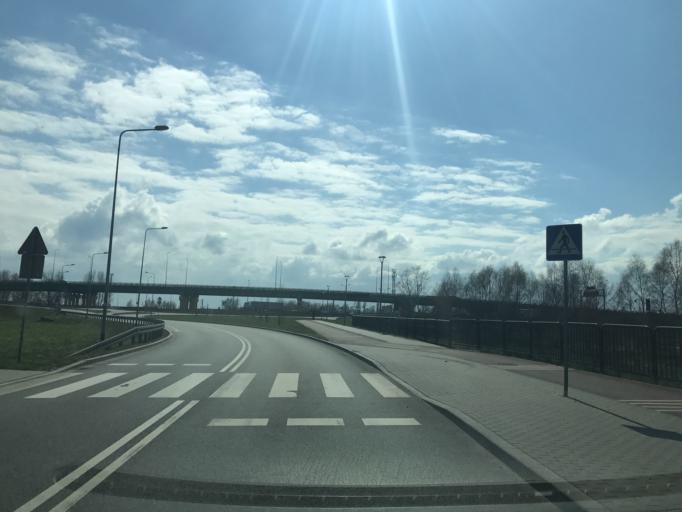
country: PL
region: Pomeranian Voivodeship
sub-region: Gdansk
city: Gdansk
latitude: 54.3799
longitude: 18.6802
